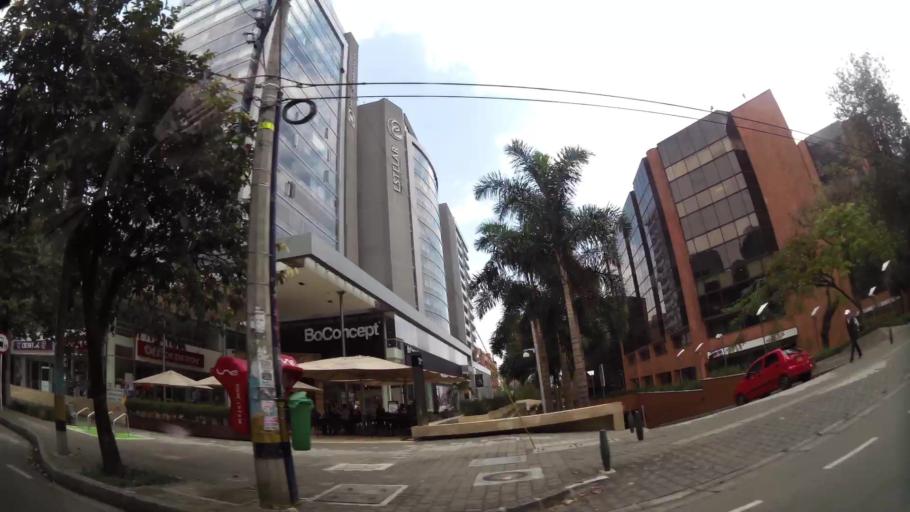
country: CO
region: Antioquia
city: Itagui
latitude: 6.2011
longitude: -75.5726
